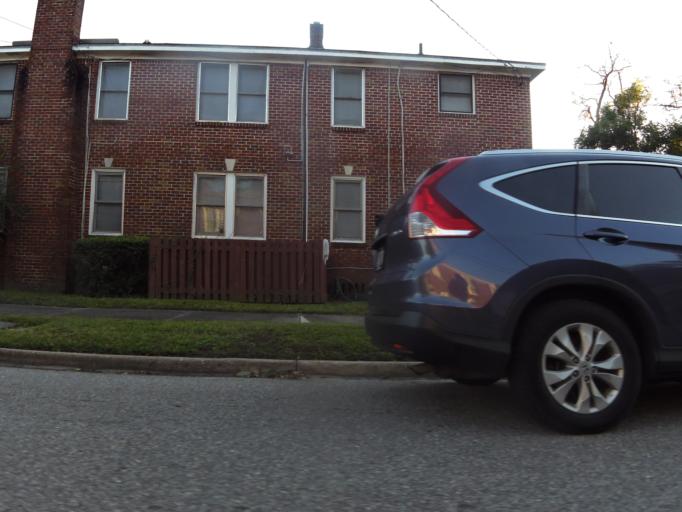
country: US
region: Florida
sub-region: Duval County
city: Jacksonville
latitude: 30.3166
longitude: -81.6930
